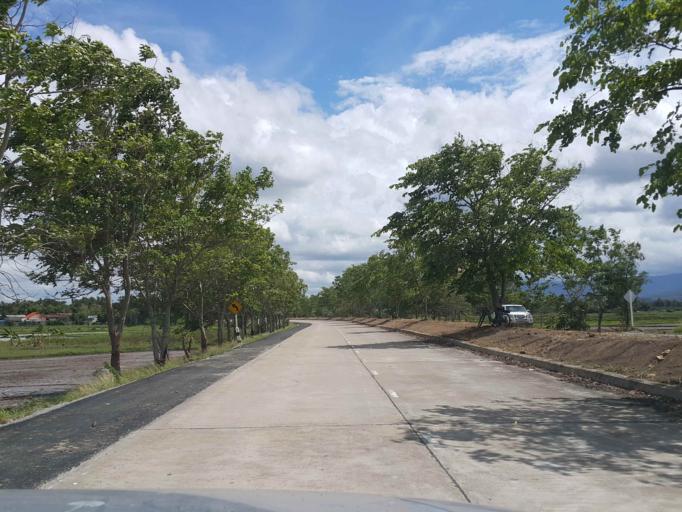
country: TH
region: Tak
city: Tak
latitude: 16.8693
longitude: 99.1136
